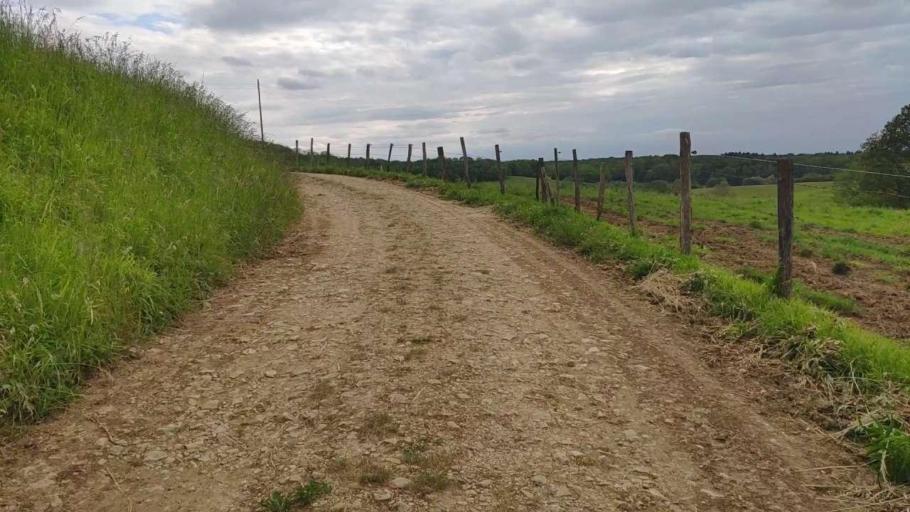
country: FR
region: Franche-Comte
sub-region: Departement du Jura
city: Bletterans
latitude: 46.7929
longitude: 5.5588
